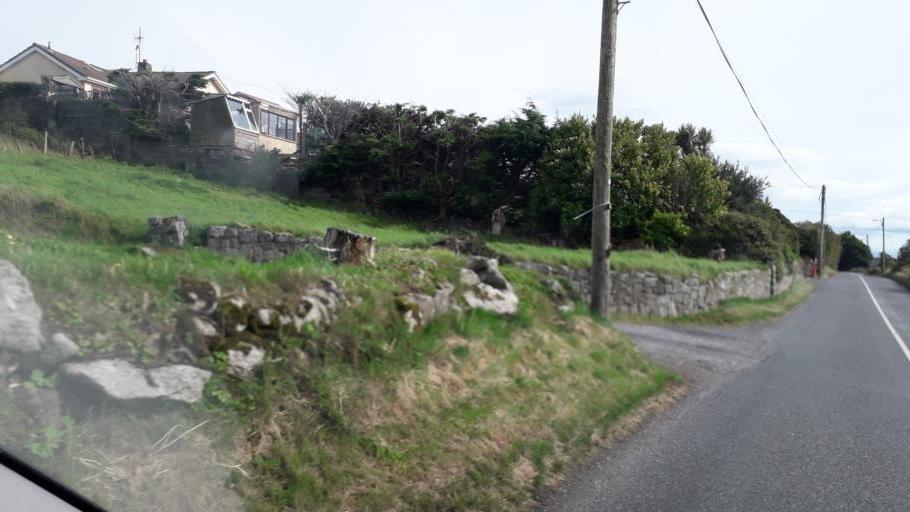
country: IE
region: Leinster
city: Balally
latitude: 53.2214
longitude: -6.2339
